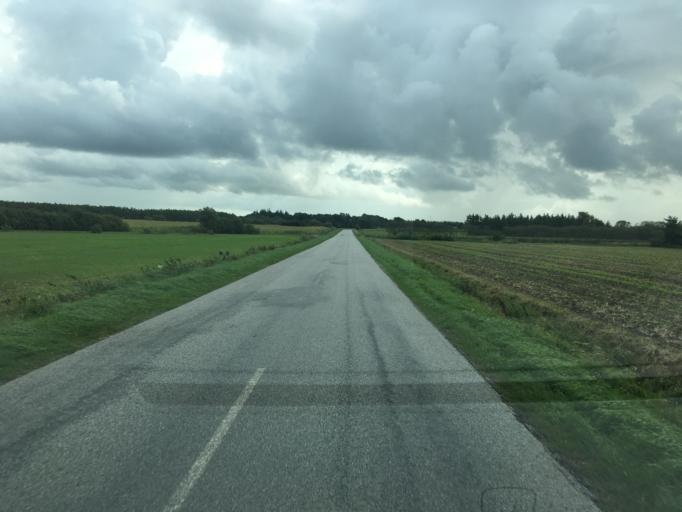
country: DK
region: South Denmark
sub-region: Tonder Kommune
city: Tonder
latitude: 54.9652
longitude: 8.8143
